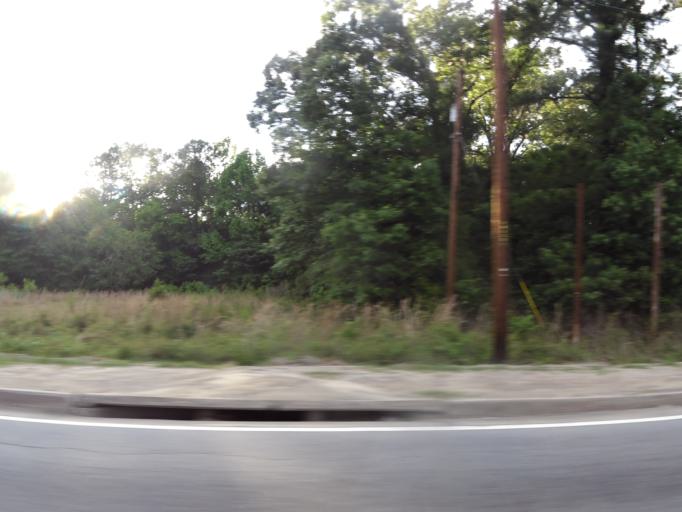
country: US
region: Georgia
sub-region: Chatham County
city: Garden City
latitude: 32.0724
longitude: -81.2003
